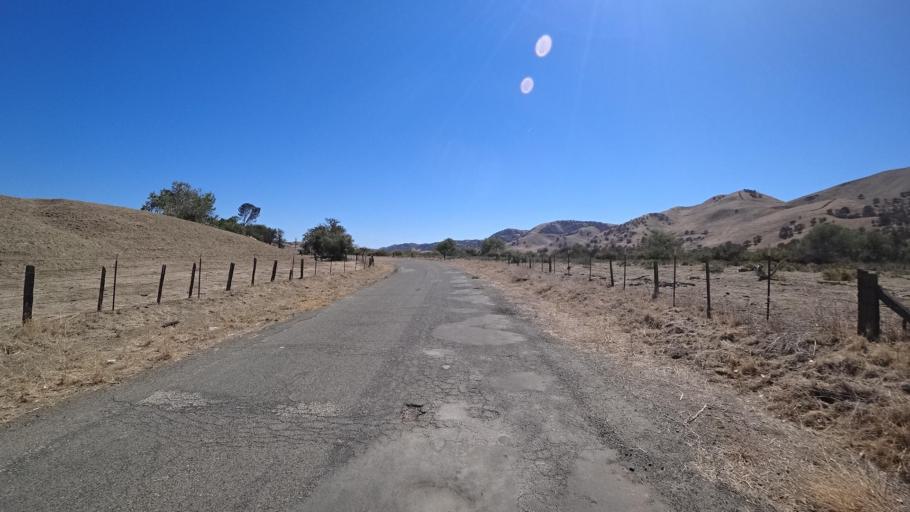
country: US
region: California
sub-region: Monterey County
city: King City
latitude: 36.2826
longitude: -120.9628
